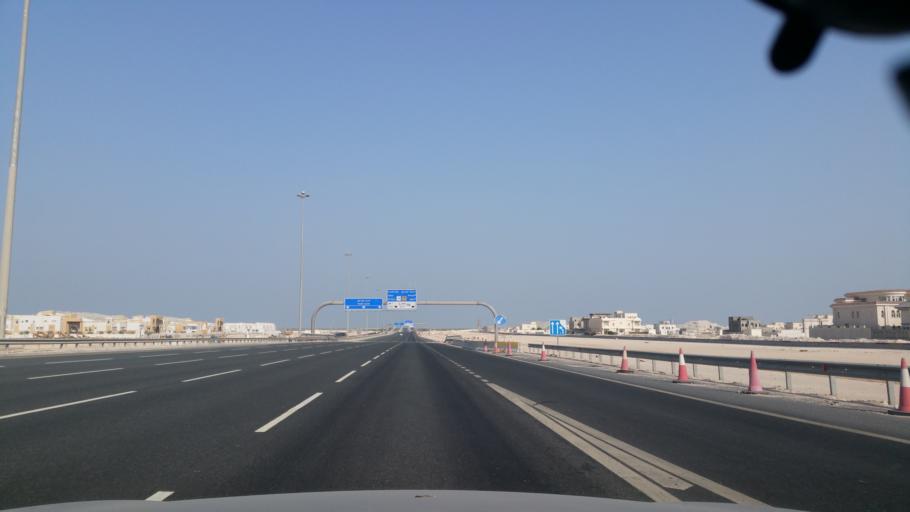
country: QA
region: Baladiyat Umm Salal
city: Umm Salal `Ali
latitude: 25.4567
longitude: 51.4583
